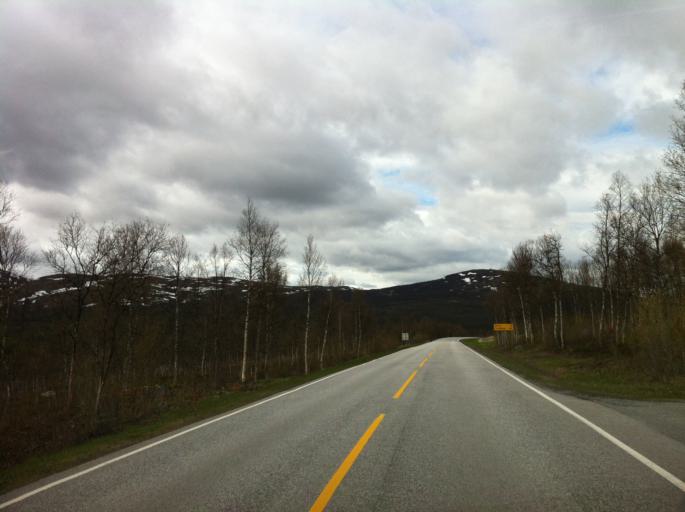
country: NO
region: Sor-Trondelag
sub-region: Roros
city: Roros
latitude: 62.5957
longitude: 11.8243
